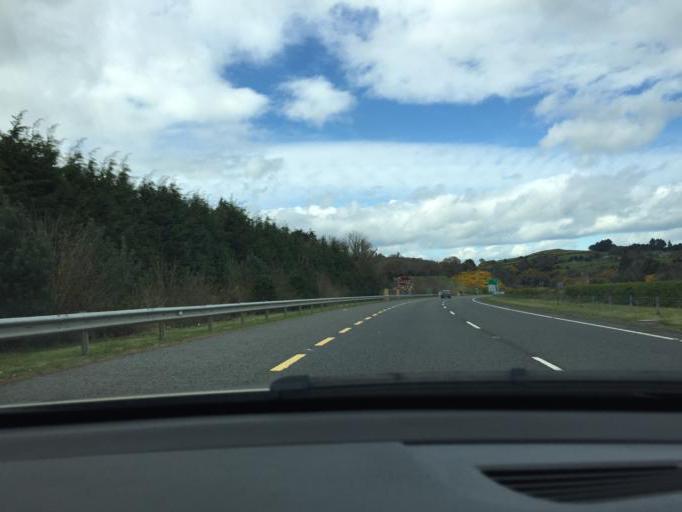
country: IE
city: Newtownmountkennedy
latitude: 53.0497
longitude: -6.0924
